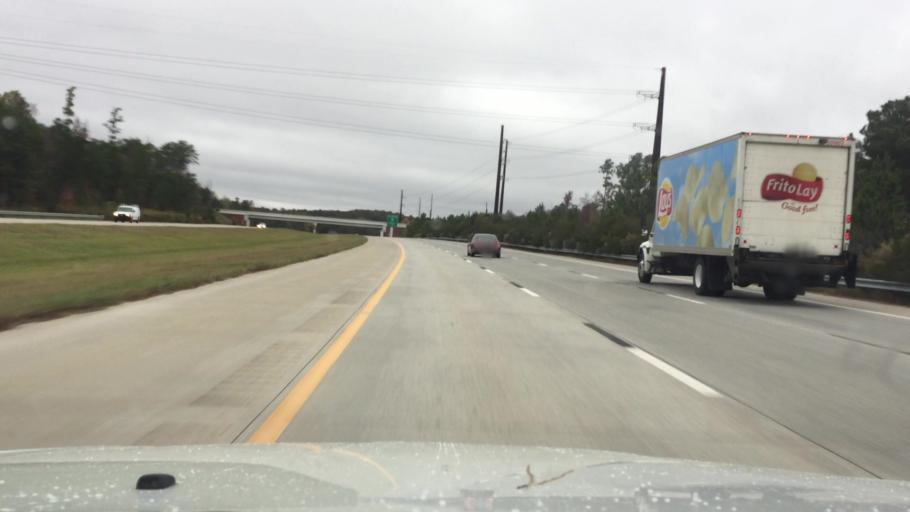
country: US
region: North Carolina
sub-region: Wake County
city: Green Level
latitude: 35.8191
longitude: -78.8922
